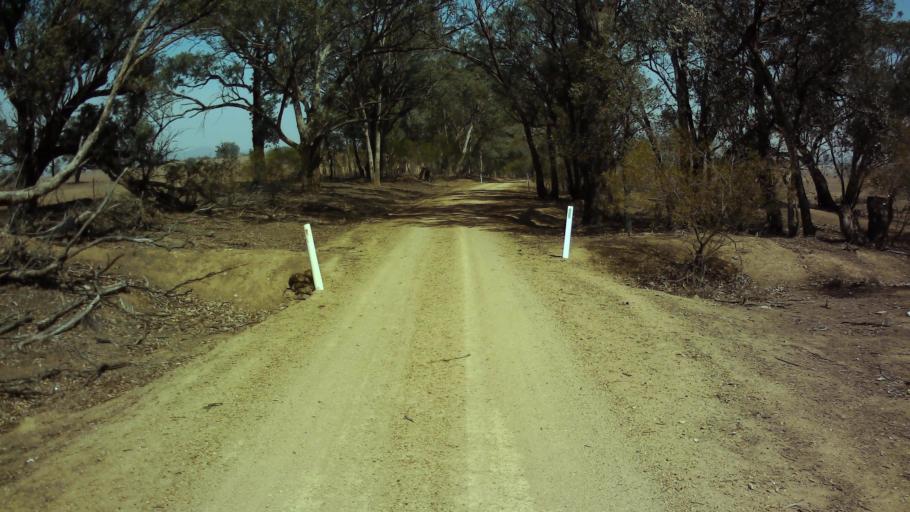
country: AU
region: New South Wales
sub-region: Weddin
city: Grenfell
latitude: -33.8972
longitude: 148.1251
